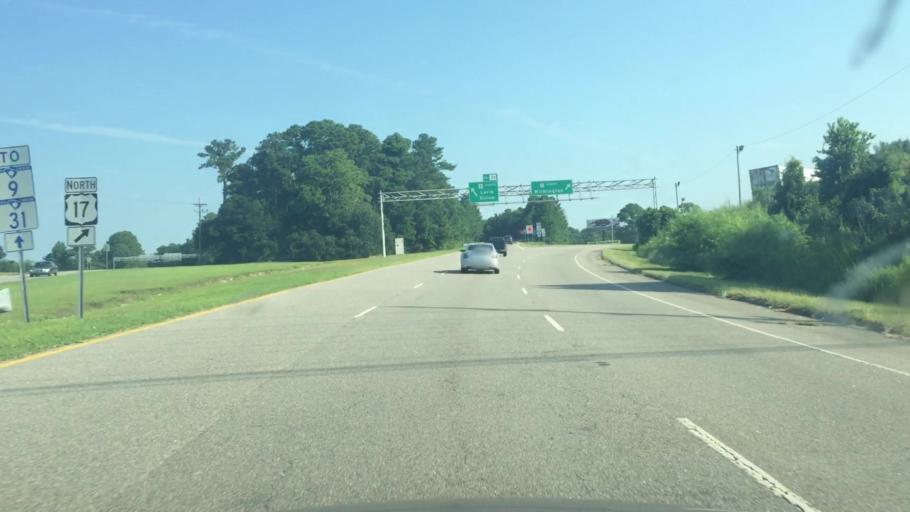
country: US
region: South Carolina
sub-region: Horry County
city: Little River
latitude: 33.8594
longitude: -78.6566
